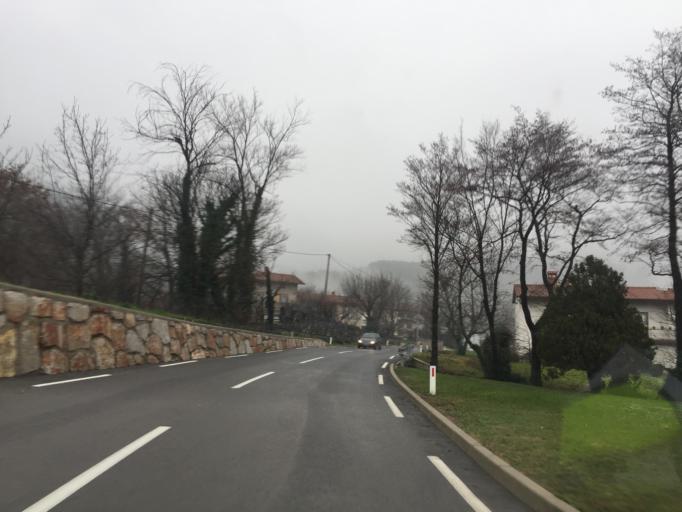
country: SI
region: Ajdovscina
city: Lokavec
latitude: 45.9092
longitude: 13.8904
